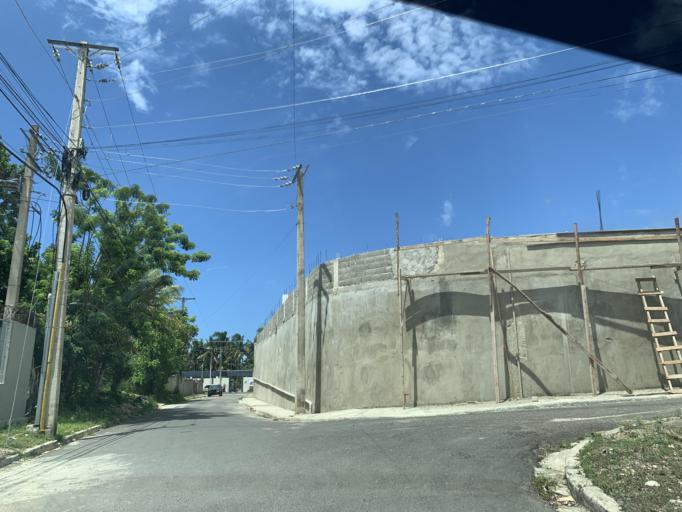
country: DO
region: Puerto Plata
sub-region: Puerto Plata
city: Puerto Plata
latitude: 19.7856
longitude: -70.6729
